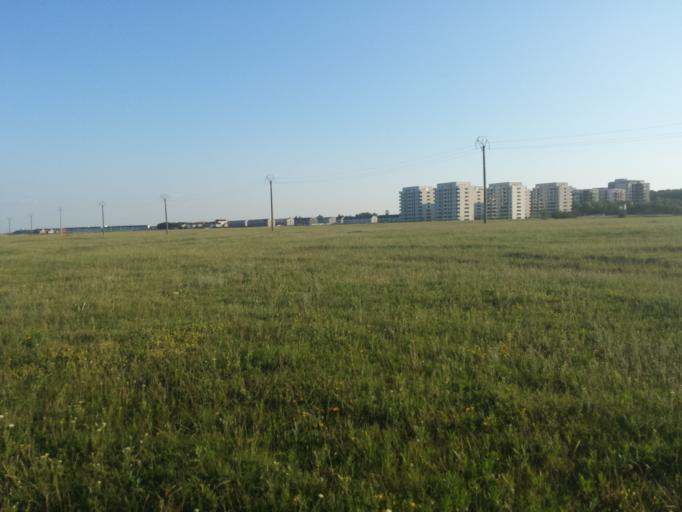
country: RO
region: Ilfov
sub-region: Comuna Tunari
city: Tunari
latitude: 44.5266
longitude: 26.1518
